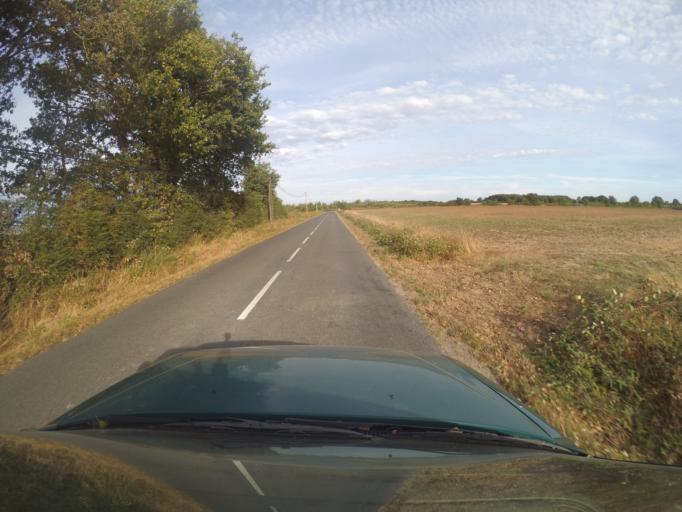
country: FR
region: Pays de la Loire
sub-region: Departement de la Loire-Atlantique
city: Saint-Hilaire-de-Clisson
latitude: 47.0618
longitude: -1.3255
